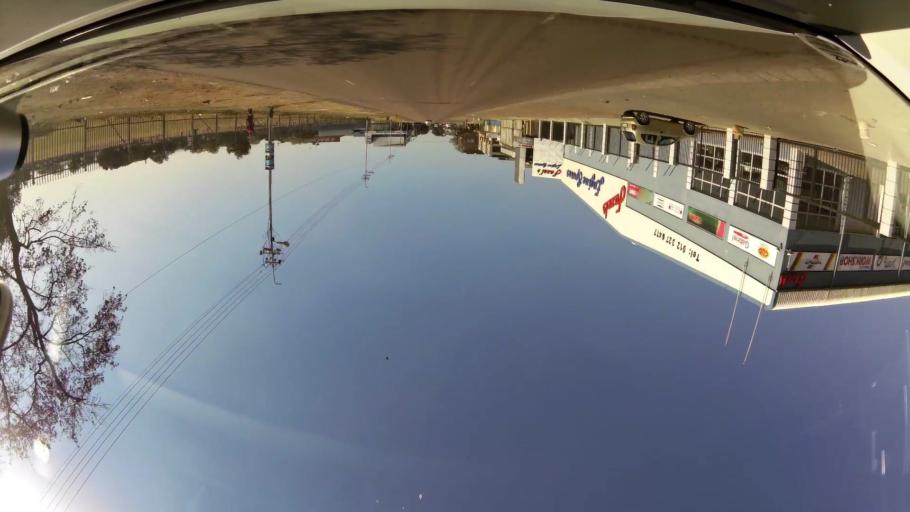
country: ZA
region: Gauteng
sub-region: City of Tshwane Metropolitan Municipality
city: Pretoria
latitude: -25.7553
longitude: 28.1522
